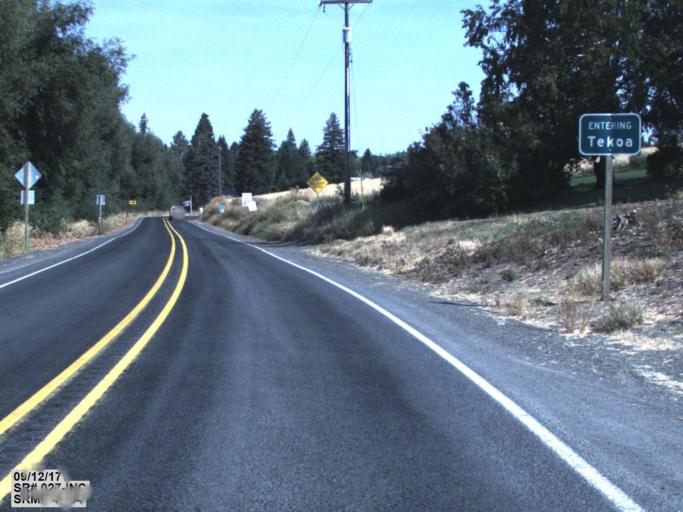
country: US
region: Idaho
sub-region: Benewah County
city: Plummer
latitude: 47.2168
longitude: -117.0775
